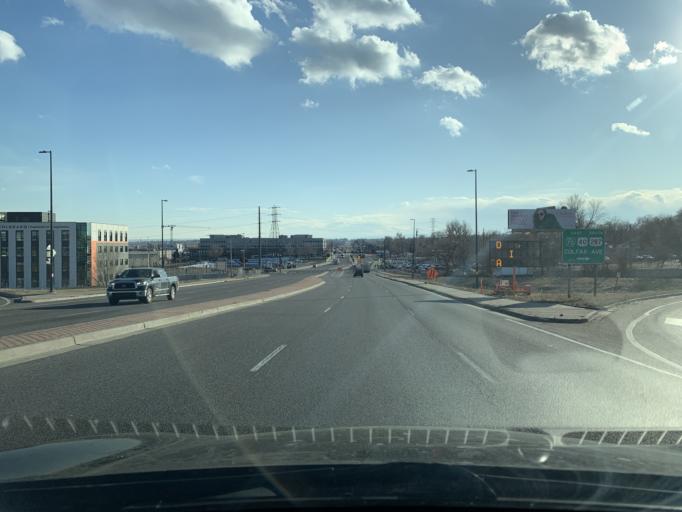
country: US
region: Colorado
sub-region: Denver County
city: Denver
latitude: 39.7398
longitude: -105.0253
